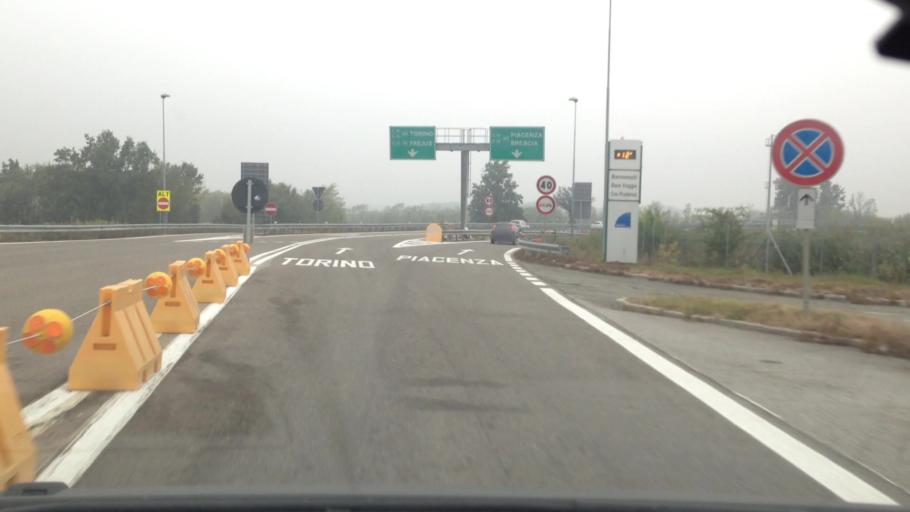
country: IT
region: Piedmont
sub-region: Provincia di Alessandria
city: Quattordio
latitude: 44.9080
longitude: 8.4083
